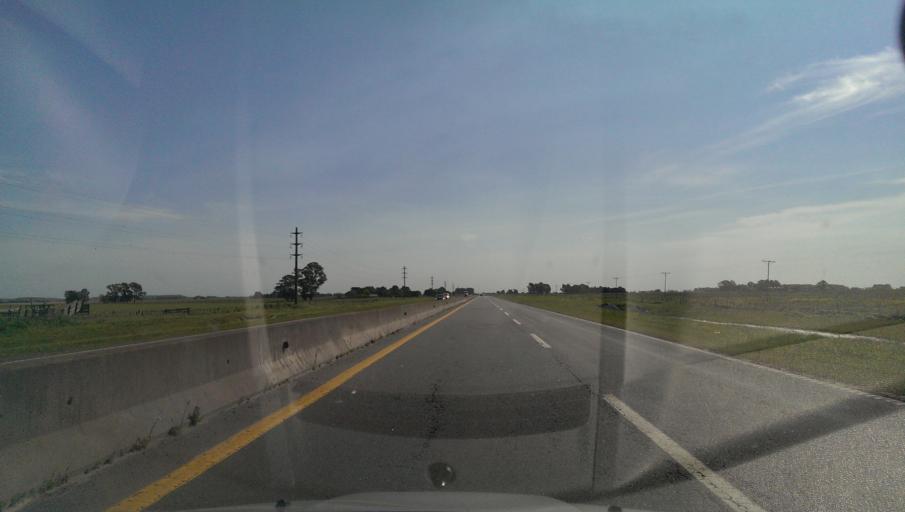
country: AR
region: Buenos Aires
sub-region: Partido de Azul
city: Azul
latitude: -36.8546
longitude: -60.0384
